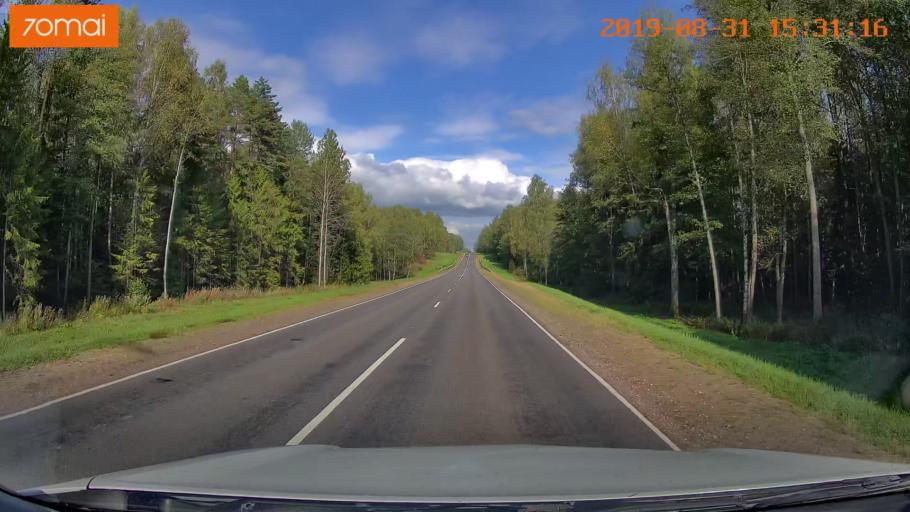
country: RU
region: Kaluga
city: Baryatino
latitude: 54.5813
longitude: 34.6505
